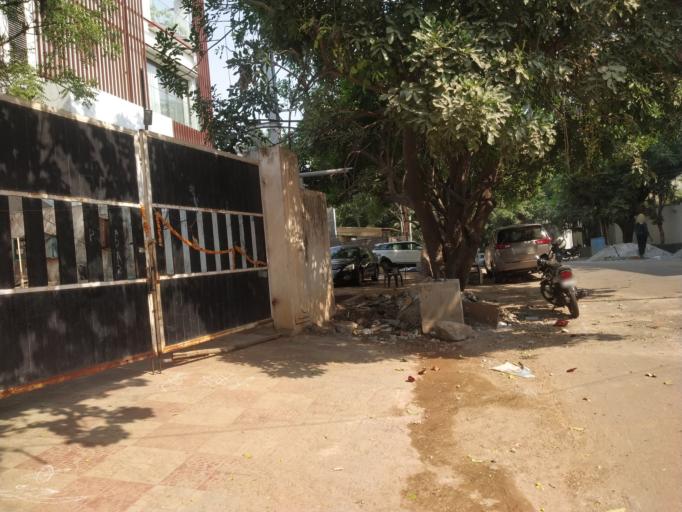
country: IN
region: Telangana
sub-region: Rangareddi
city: Kukatpalli
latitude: 17.4386
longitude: 78.4058
